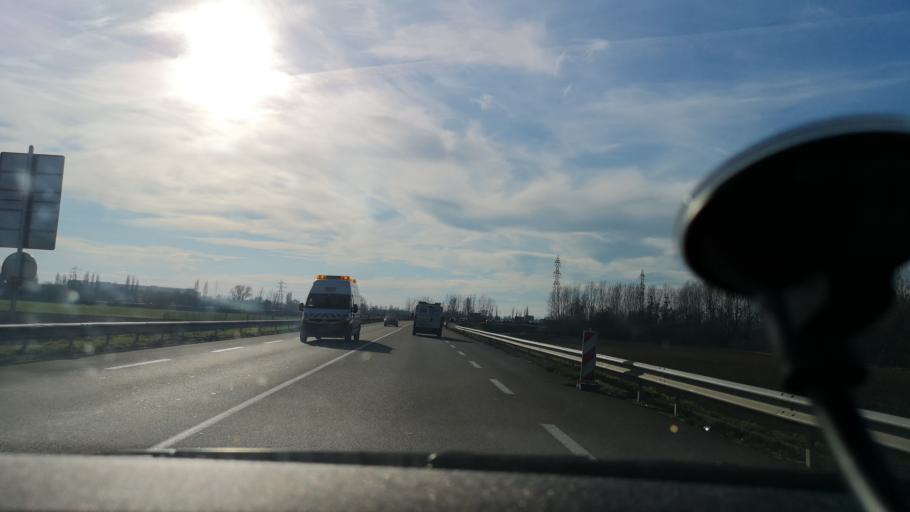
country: FR
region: Bourgogne
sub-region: Departement de Saone-et-Loire
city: Saint-Marcel
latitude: 46.7811
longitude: 4.8844
